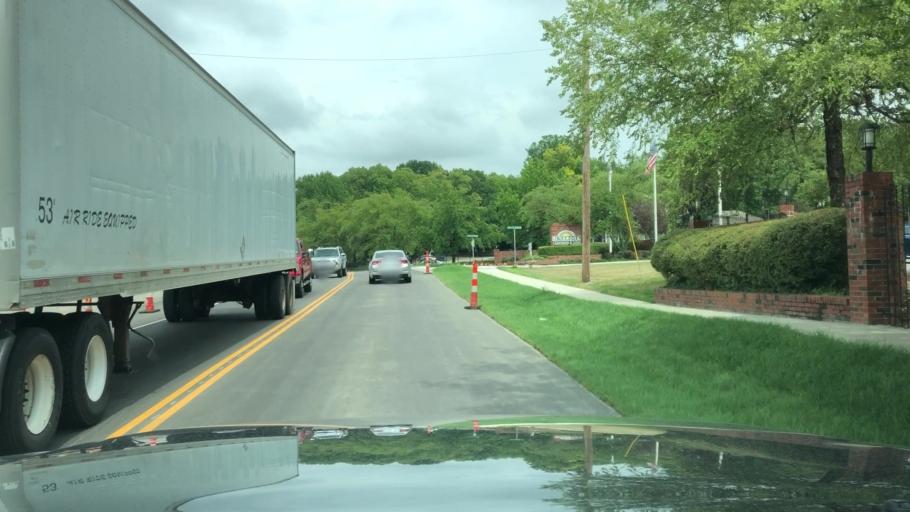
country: US
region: Missouri
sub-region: Saint Charles County
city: Saint Peters
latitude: 38.7981
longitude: -90.5590
